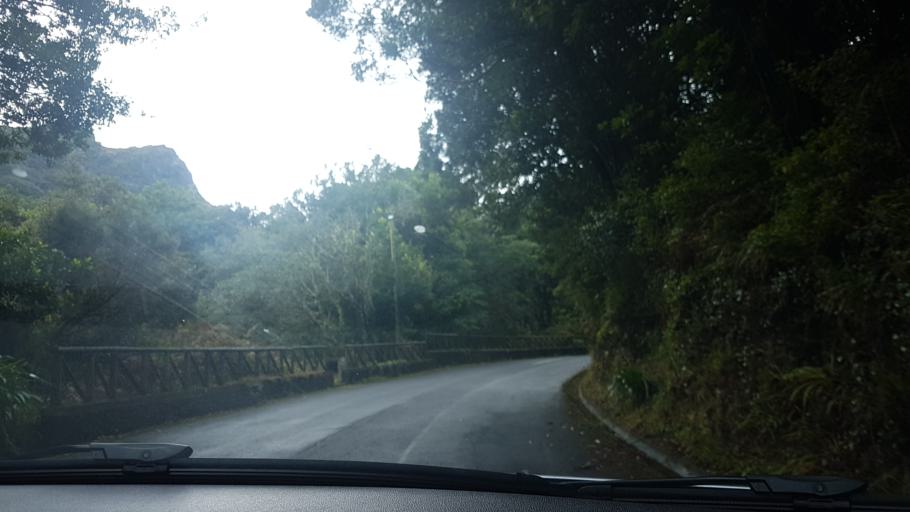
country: PT
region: Madeira
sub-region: Sao Vicente
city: Sao Vicente
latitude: 32.7612
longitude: -17.0159
